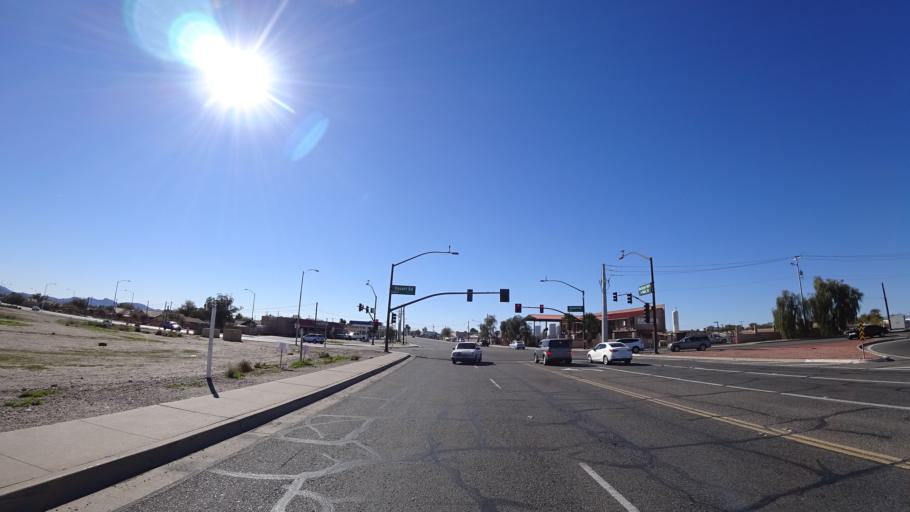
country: US
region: Arizona
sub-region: Maricopa County
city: Avondale
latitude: 33.4341
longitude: -112.3404
